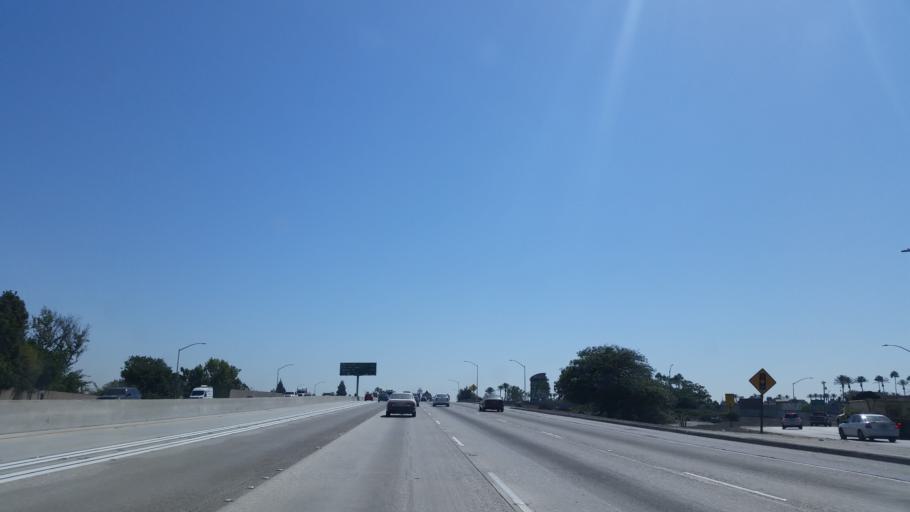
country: US
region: California
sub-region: Los Angeles County
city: Hawaiian Gardens
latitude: 33.8337
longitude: -118.0856
